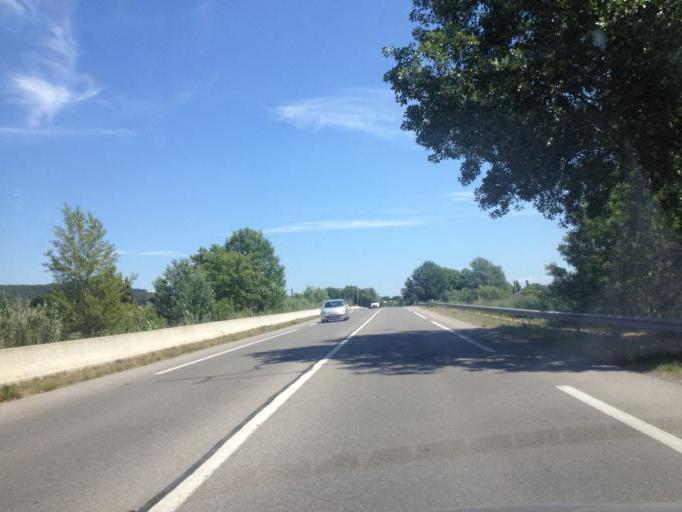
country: FR
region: Provence-Alpes-Cote d'Azur
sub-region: Departement du Vaucluse
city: Lauris
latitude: 43.7396
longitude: 5.3301
